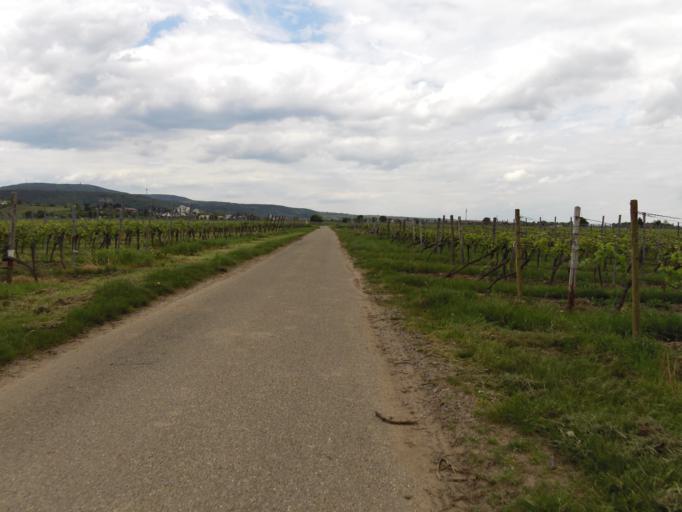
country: DE
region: Rheinland-Pfalz
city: Wachenheim
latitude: 49.4483
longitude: 8.1842
